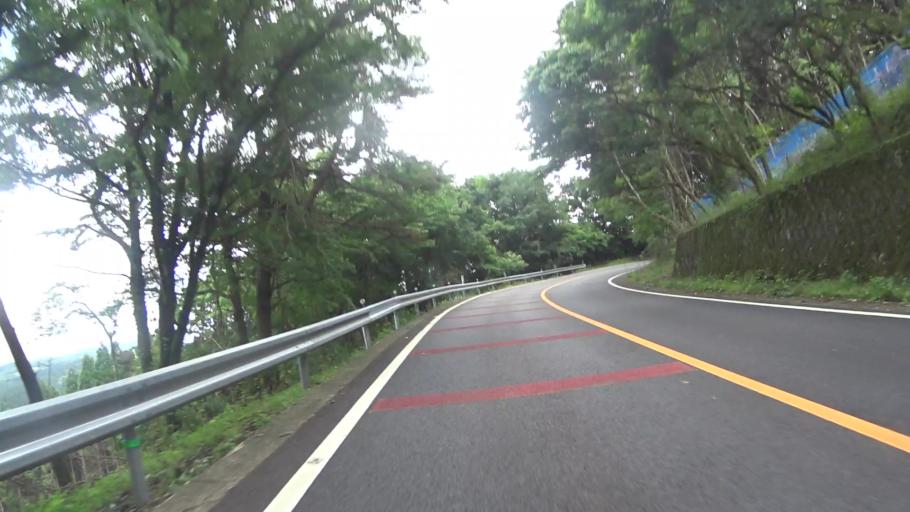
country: JP
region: Oita
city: Tsukawaki
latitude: 33.1996
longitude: 131.2875
